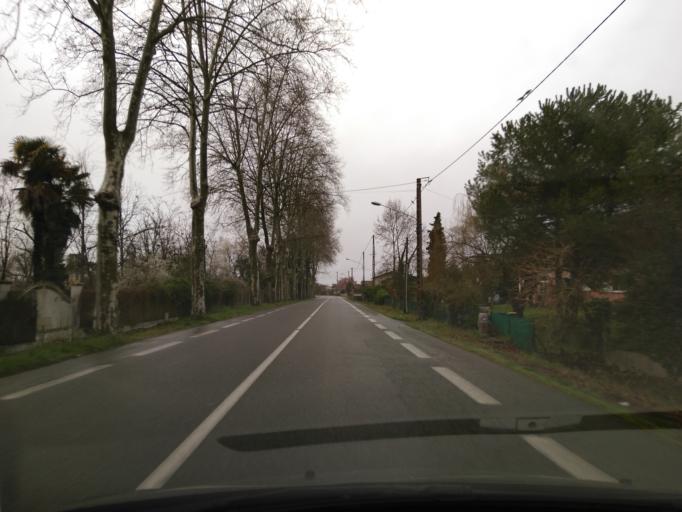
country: FR
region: Midi-Pyrenees
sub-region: Departement de la Haute-Garonne
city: Rieux-Volvestre
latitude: 43.2509
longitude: 1.2017
